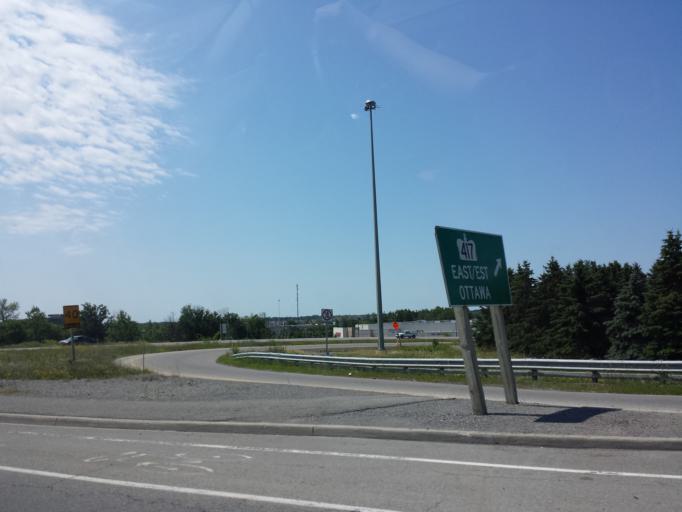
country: CA
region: Ontario
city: Bells Corners
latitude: 45.3047
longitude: -75.9107
